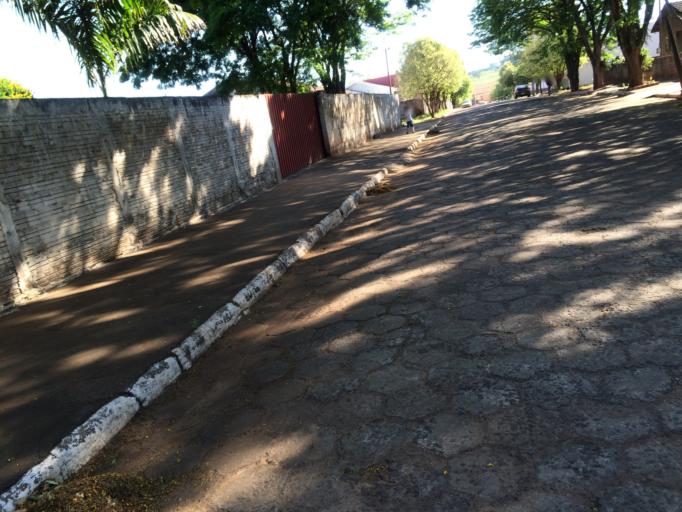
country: BR
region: Parana
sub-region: Cianorte
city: Cianorte
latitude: -23.5386
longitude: -52.5926
